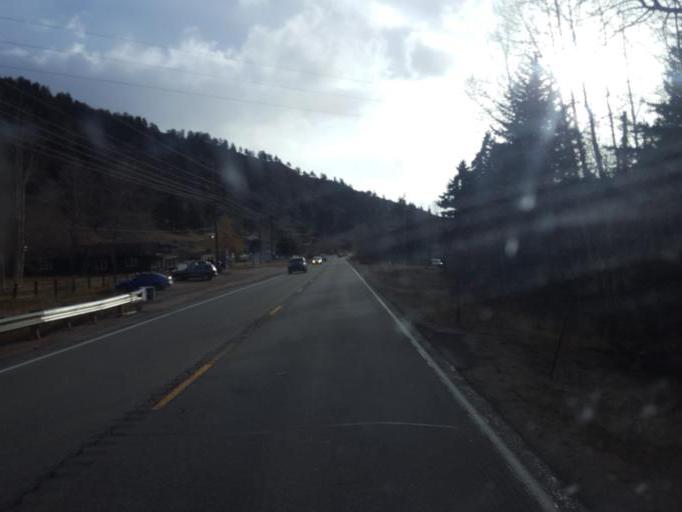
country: US
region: Colorado
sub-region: Clear Creek County
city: Georgetown
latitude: 39.4557
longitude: -105.6477
